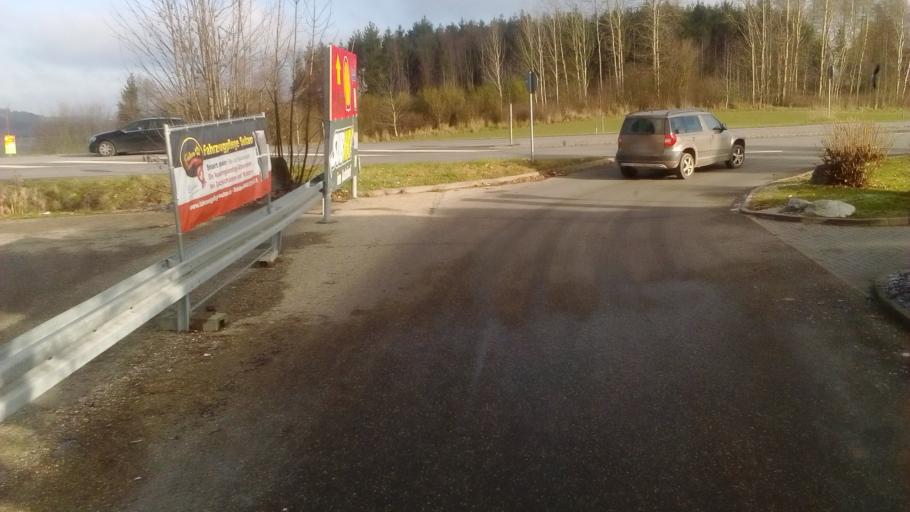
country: DE
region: Bavaria
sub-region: Upper Bavaria
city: Paunzhausen
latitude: 48.5089
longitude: 11.5838
